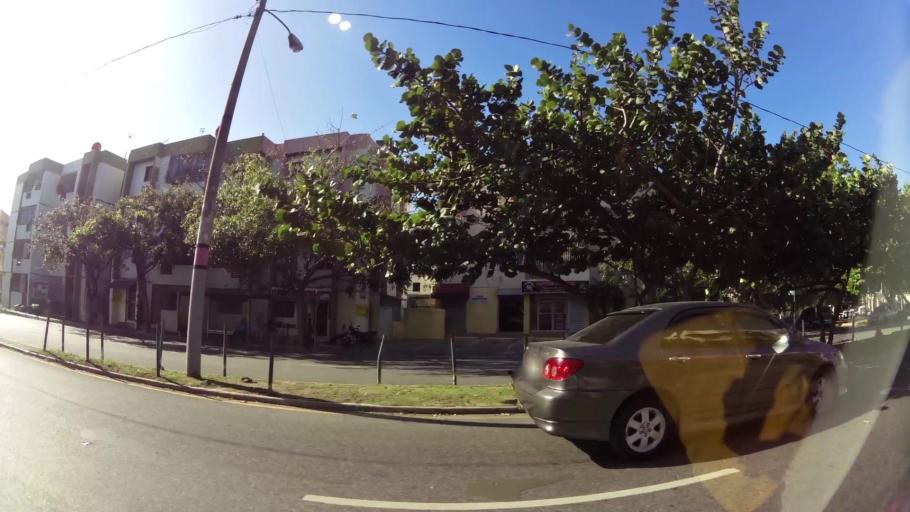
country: DO
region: Nacional
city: San Carlos
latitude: 18.4768
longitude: -69.8958
